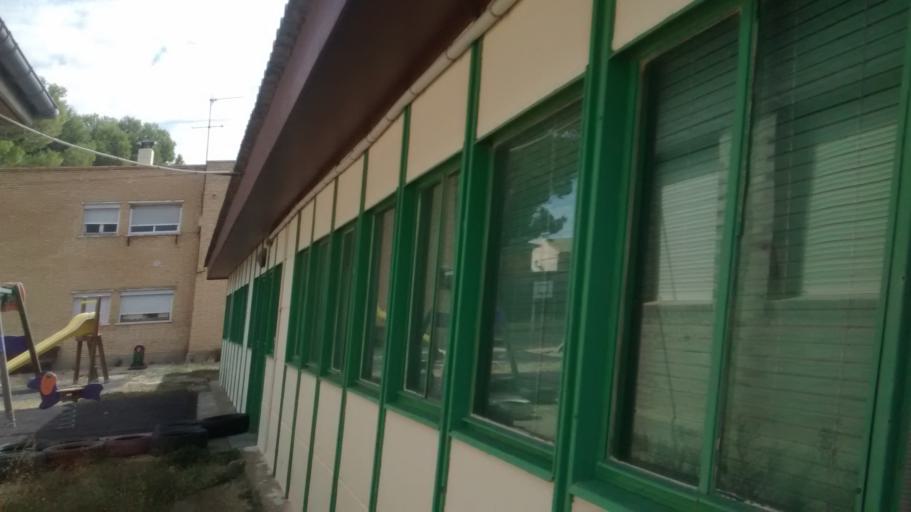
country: ES
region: Aragon
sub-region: Provincia de Zaragoza
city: Villanueva de Gallego
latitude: 41.7591
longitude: -0.7980
